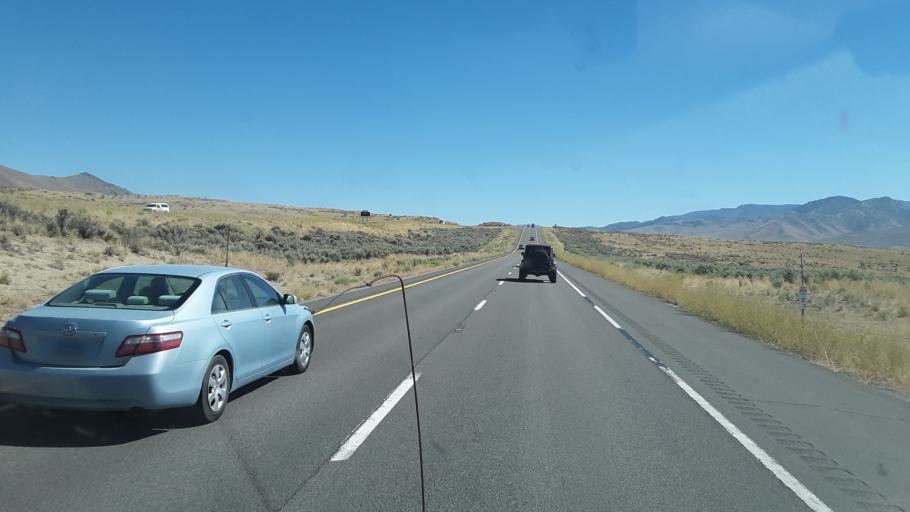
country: US
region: Nevada
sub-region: Washoe County
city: Cold Springs
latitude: 39.7665
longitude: -120.0393
